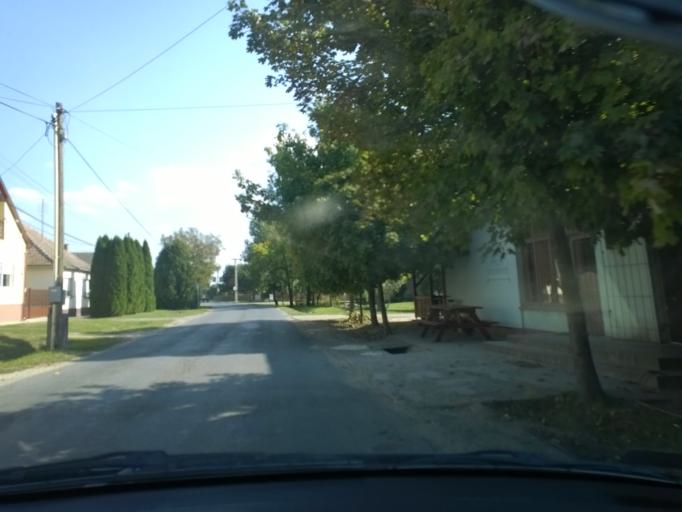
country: HU
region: Bacs-Kiskun
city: Kalocsa
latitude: 46.4865
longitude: 19.0740
